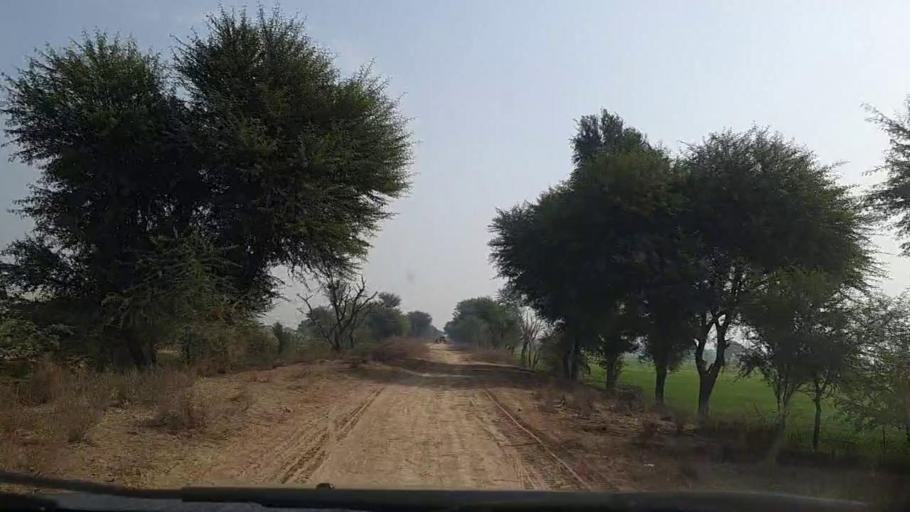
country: PK
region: Sindh
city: Sanghar
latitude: 26.0519
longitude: 68.9791
